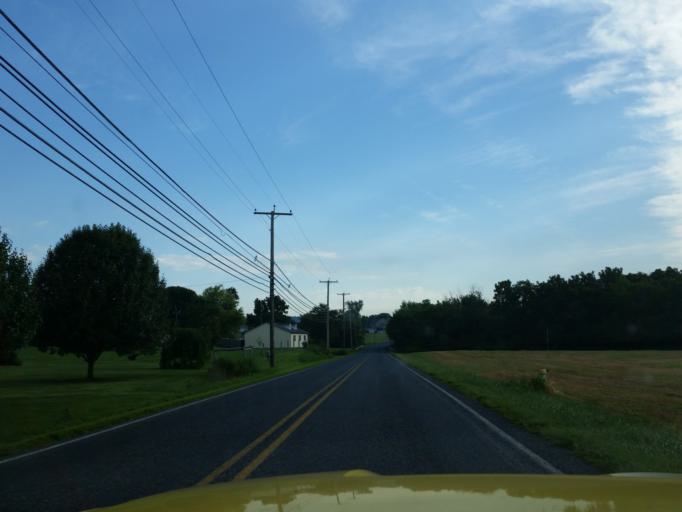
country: US
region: Pennsylvania
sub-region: Lebanon County
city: Fredericksburg
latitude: 40.4321
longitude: -76.4536
